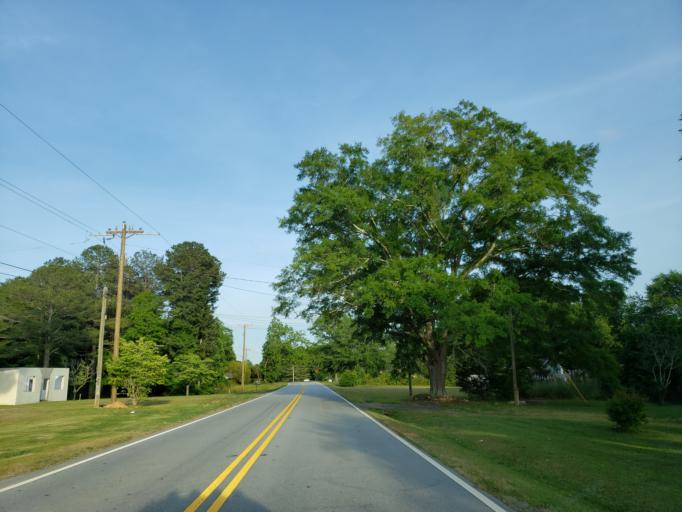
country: US
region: Georgia
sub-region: Carroll County
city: Mount Zion
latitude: 33.6094
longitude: -85.1527
